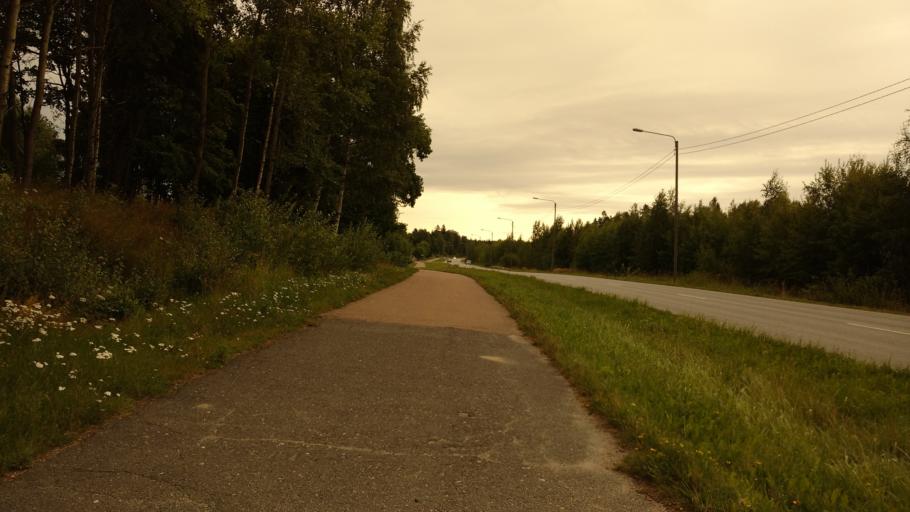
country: FI
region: Varsinais-Suomi
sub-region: Turku
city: Kaarina
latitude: 60.4431
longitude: 22.3882
